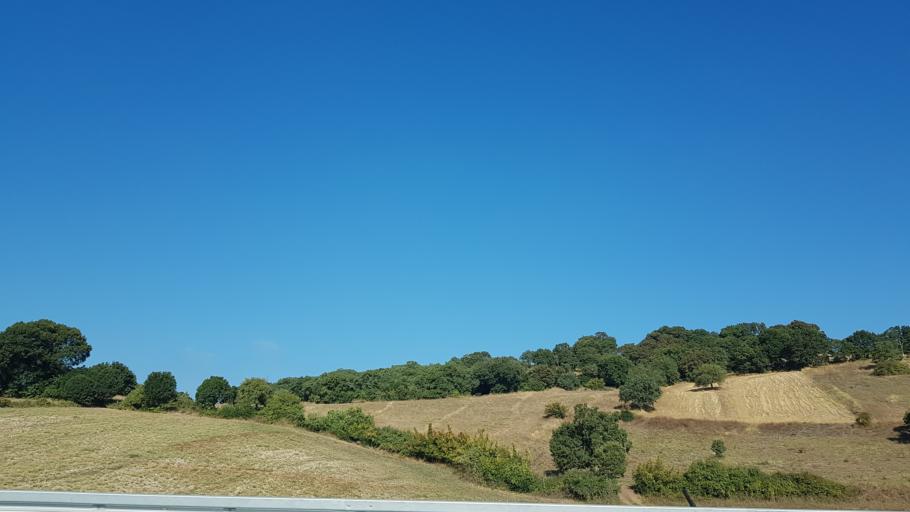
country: TR
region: Balikesir
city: Ertugrul
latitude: 39.5841
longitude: 27.6972
